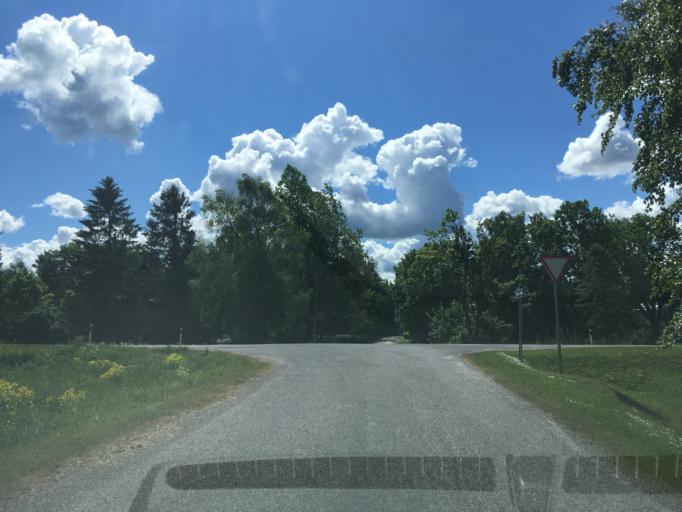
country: EE
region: Harju
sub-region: Nissi vald
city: Turba
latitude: 58.9177
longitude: 24.1668
